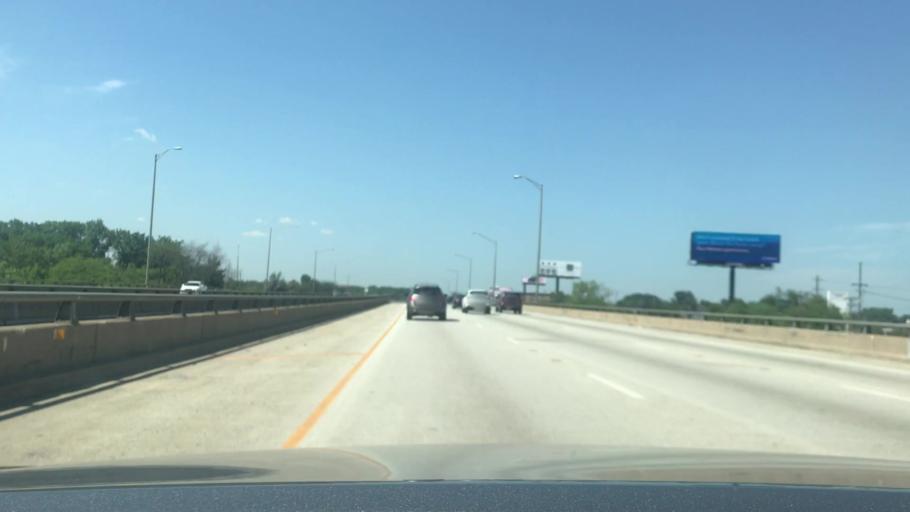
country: US
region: Illinois
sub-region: Cook County
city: Calumet Park
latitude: 41.6546
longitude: -87.6616
